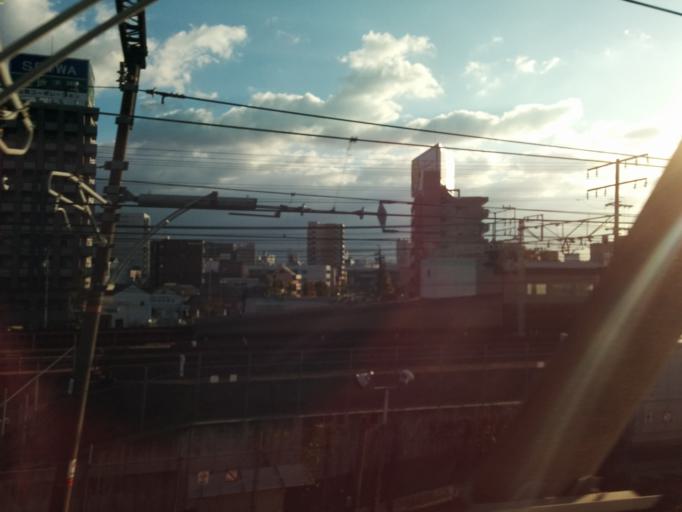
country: JP
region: Aichi
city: Nagoya-shi
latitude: 35.1526
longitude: 136.8879
